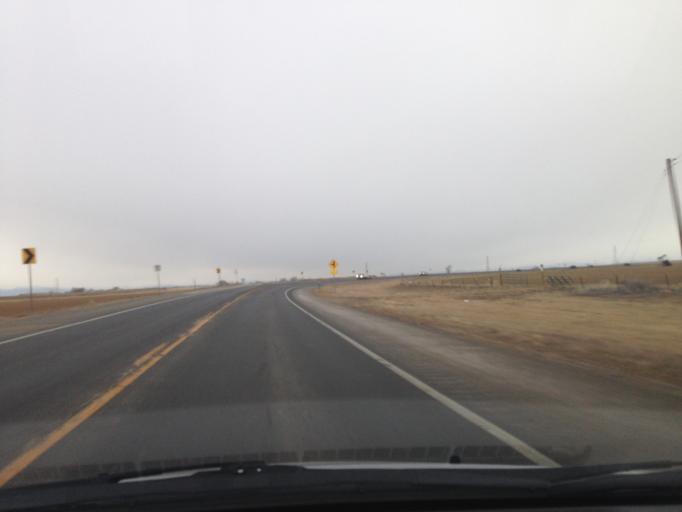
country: US
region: Colorado
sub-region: Weld County
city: Dacono
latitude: 40.0800
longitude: -104.8991
